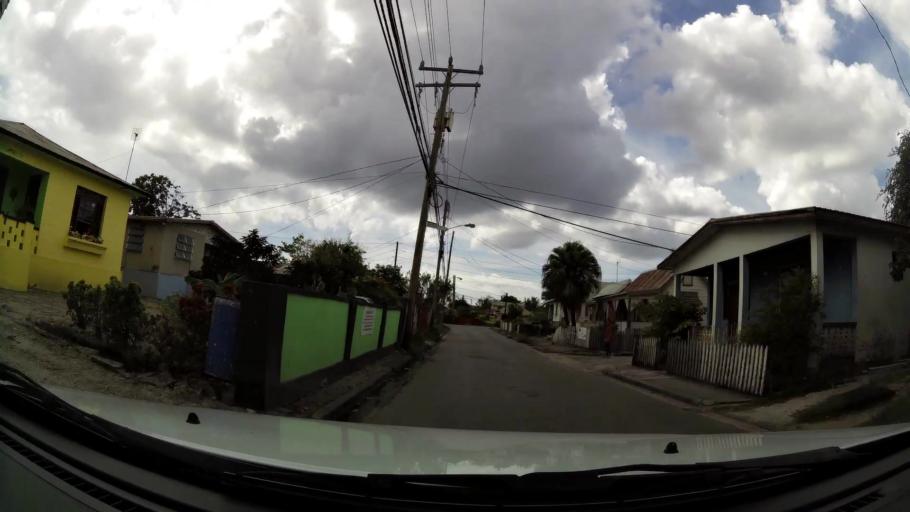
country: BB
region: Saint Michael
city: Bridgetown
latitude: 13.1146
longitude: -59.6243
